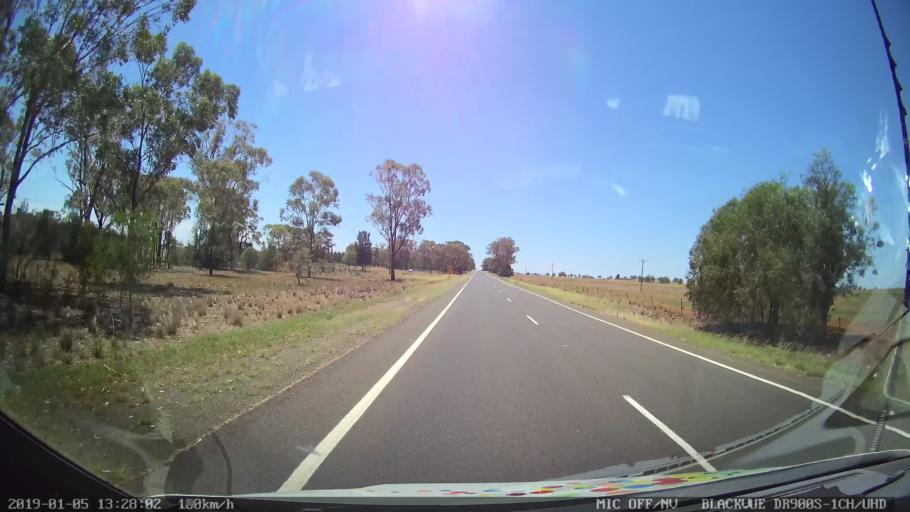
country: AU
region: New South Wales
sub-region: Gunnedah
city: Gunnedah
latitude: -31.0392
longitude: 150.0379
